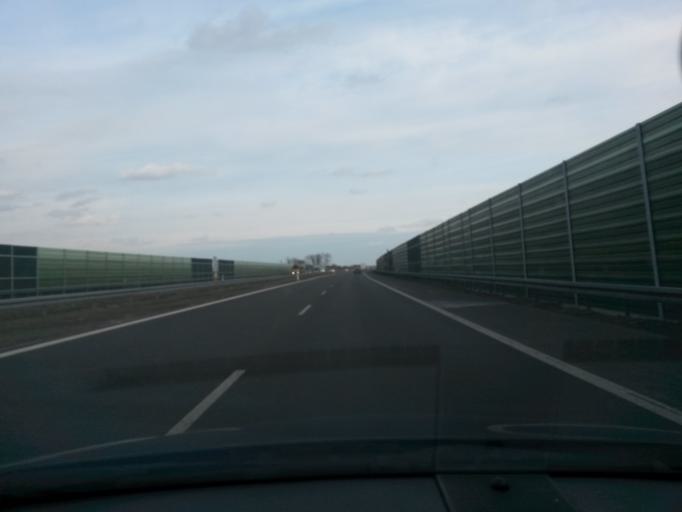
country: PL
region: Greater Poland Voivodeship
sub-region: Powiat kolski
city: Dabie
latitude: 52.1120
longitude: 18.7393
